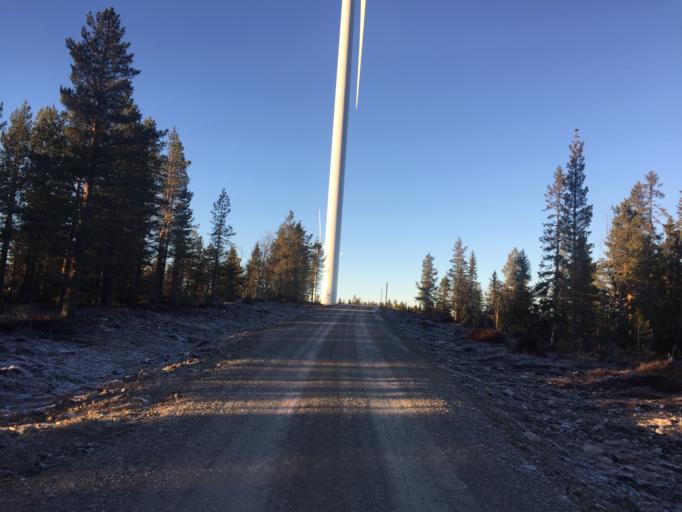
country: NO
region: Hedmark
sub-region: Elverum
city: Elverum
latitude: 61.2072
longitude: 11.7884
